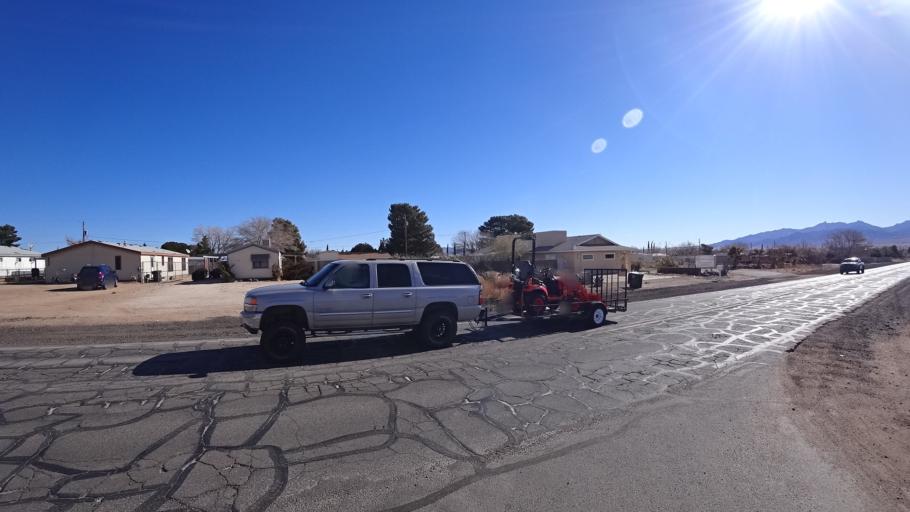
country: US
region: Arizona
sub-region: Mohave County
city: New Kingman-Butler
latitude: 35.2718
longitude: -114.0453
